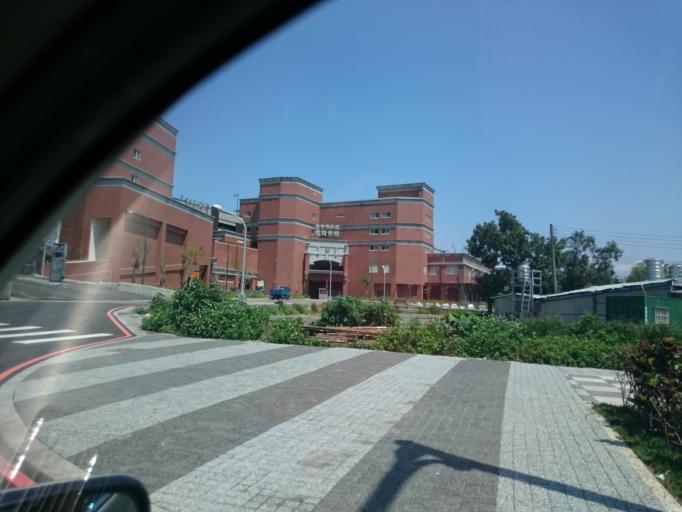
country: TW
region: Taiwan
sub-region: Taichung City
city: Taichung
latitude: 24.1336
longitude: 120.6933
